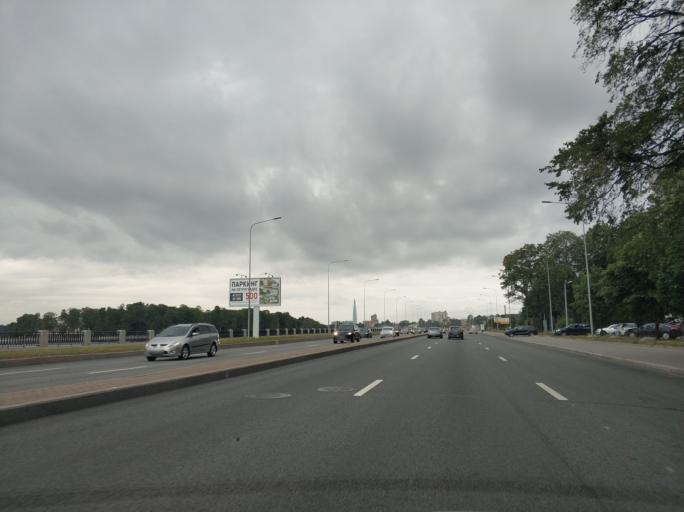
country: RU
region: Leningrad
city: Chernaya Rechka
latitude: 59.9817
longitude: 30.3131
